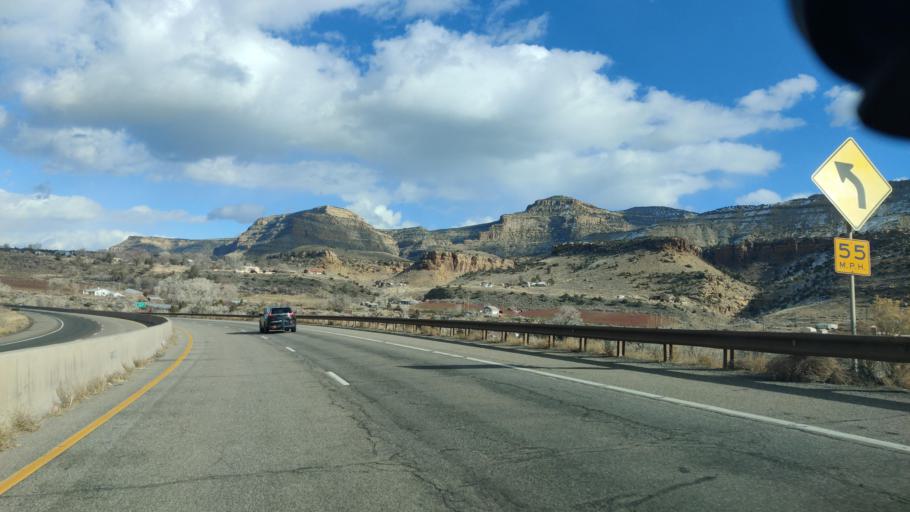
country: US
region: Colorado
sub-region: Mesa County
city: Palisade
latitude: 39.1200
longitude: -108.3247
